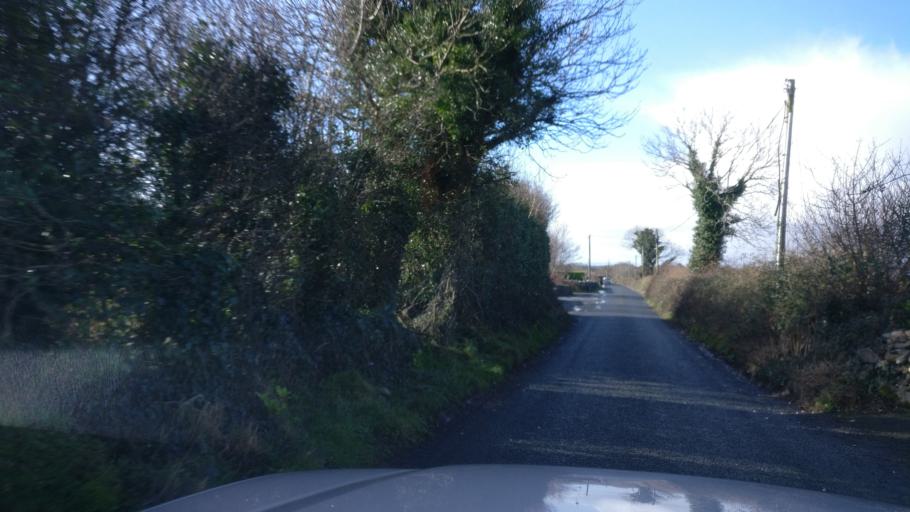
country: IE
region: Connaught
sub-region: County Galway
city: Athenry
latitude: 53.2447
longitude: -8.7669
